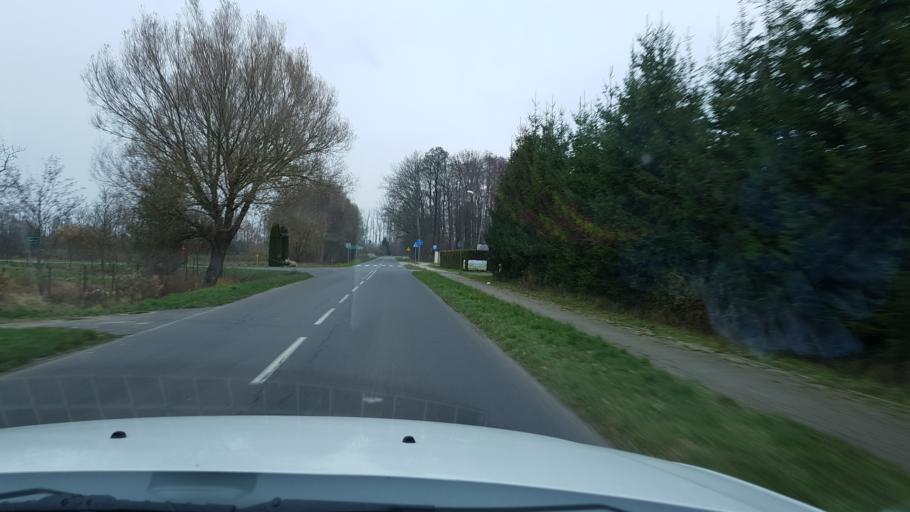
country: PL
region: West Pomeranian Voivodeship
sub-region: Powiat kamienski
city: Kamien Pomorski
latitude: 53.9493
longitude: 14.6799
